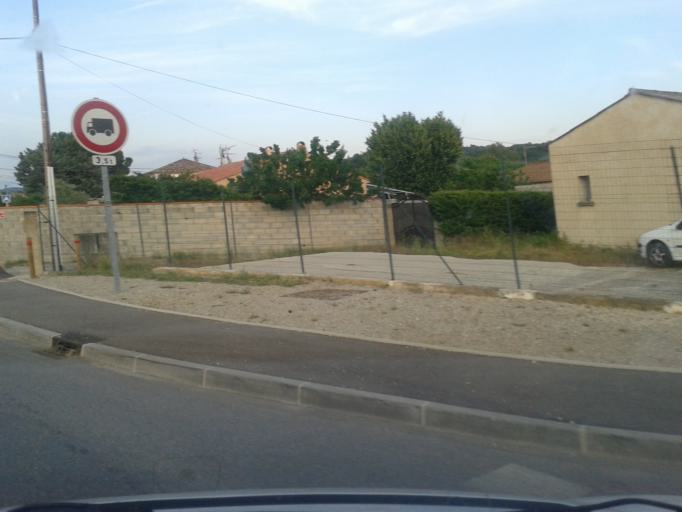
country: FR
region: Provence-Alpes-Cote d'Azur
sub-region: Departement du Var
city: Vinon-sur-Verdon
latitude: 43.7296
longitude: 5.8067
